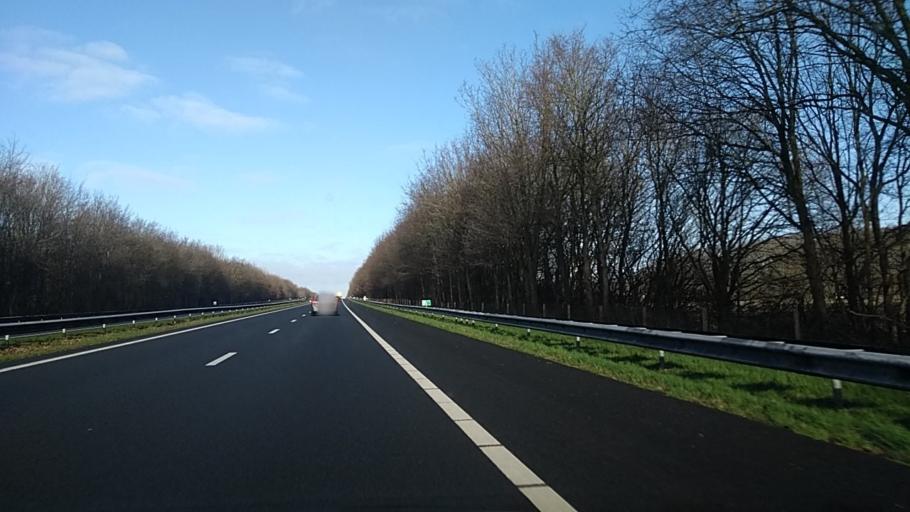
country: NL
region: Overijssel
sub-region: Gemeente Steenwijkerland
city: Steenwijkerwold
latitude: 52.8235
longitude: 6.0696
